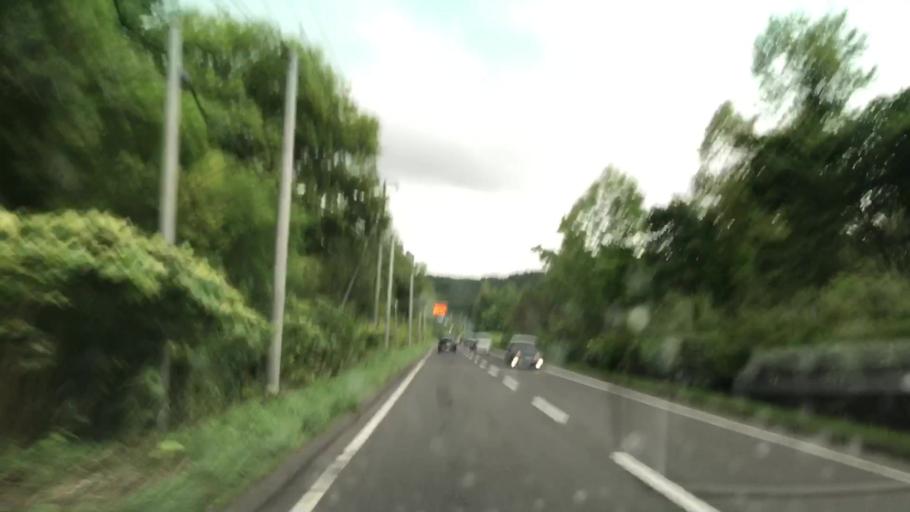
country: JP
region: Hokkaido
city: Niseko Town
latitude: 42.8255
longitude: 141.0048
